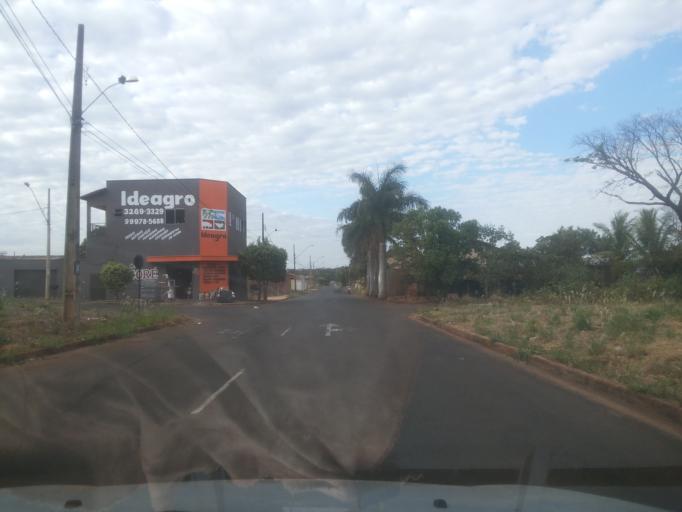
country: BR
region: Minas Gerais
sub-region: Ituiutaba
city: Ituiutaba
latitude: -18.9980
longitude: -49.4562
